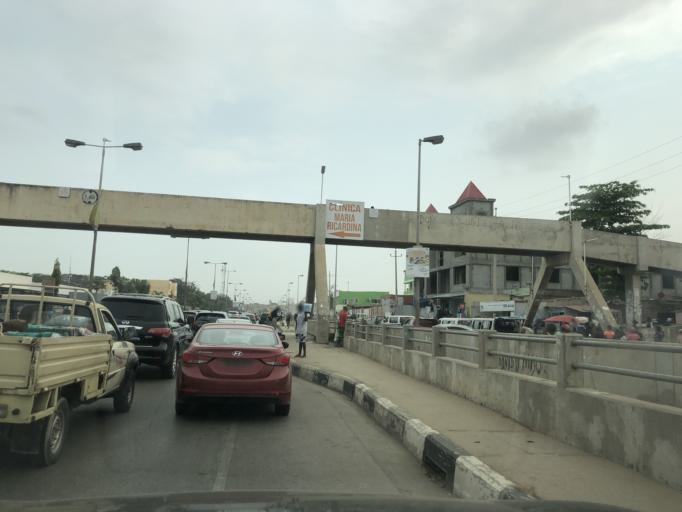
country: AO
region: Luanda
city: Luanda
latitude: -8.8523
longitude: 13.2092
